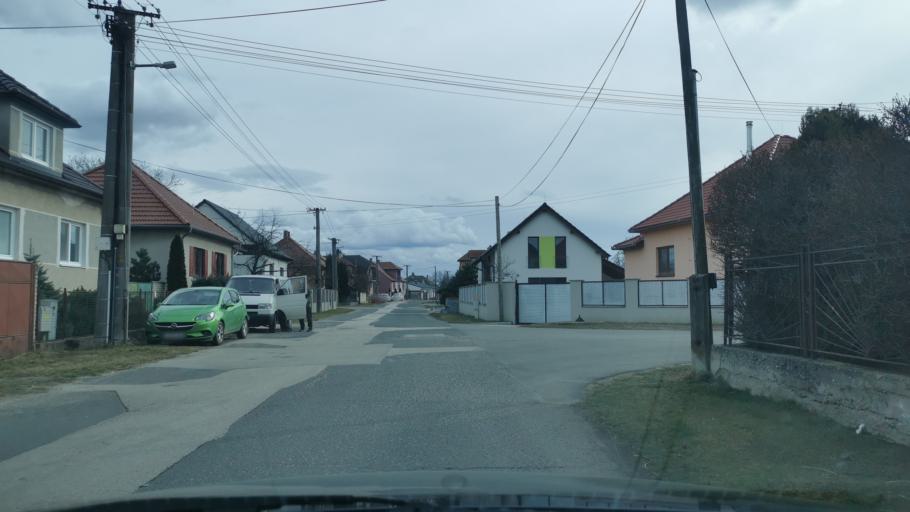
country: CZ
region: South Moravian
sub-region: Okres Breclav
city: Lanzhot
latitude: 48.6913
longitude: 17.0217
